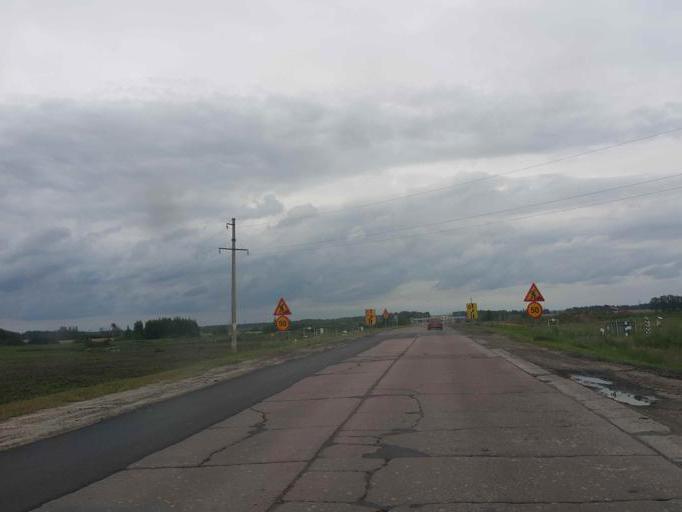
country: RU
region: Tambov
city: Zavoronezhskoye
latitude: 52.8915
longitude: 40.6961
